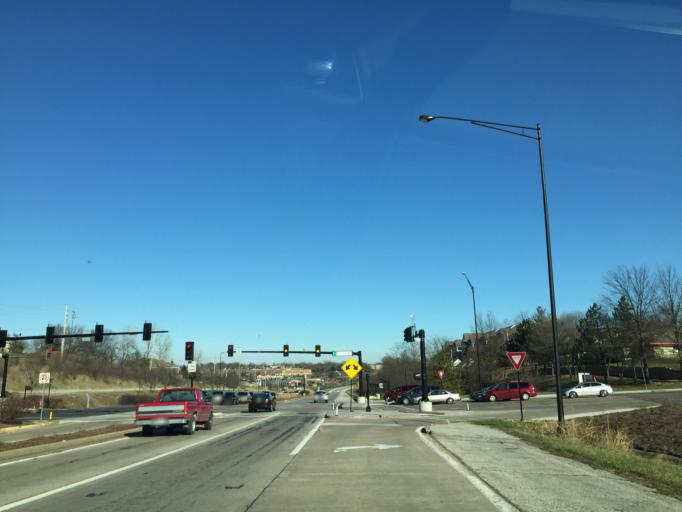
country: US
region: Missouri
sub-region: Saint Louis County
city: Ellisville
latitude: 38.5831
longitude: -90.6158
